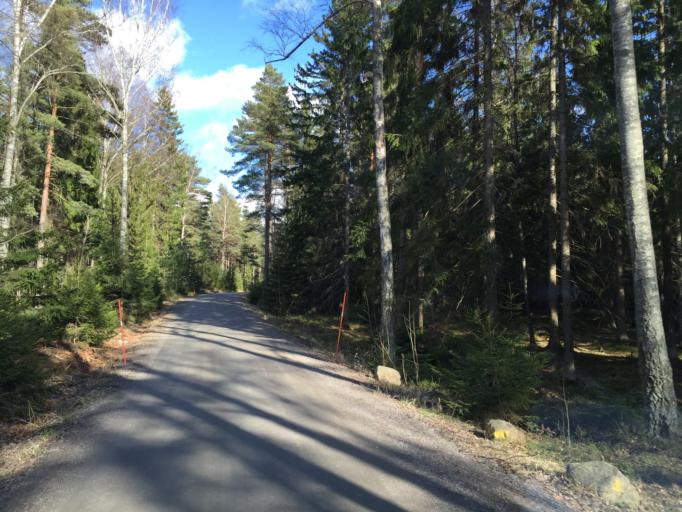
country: SE
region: Stockholm
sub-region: Sodertalje Kommun
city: Soedertaelje
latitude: 59.2352
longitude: 17.5388
